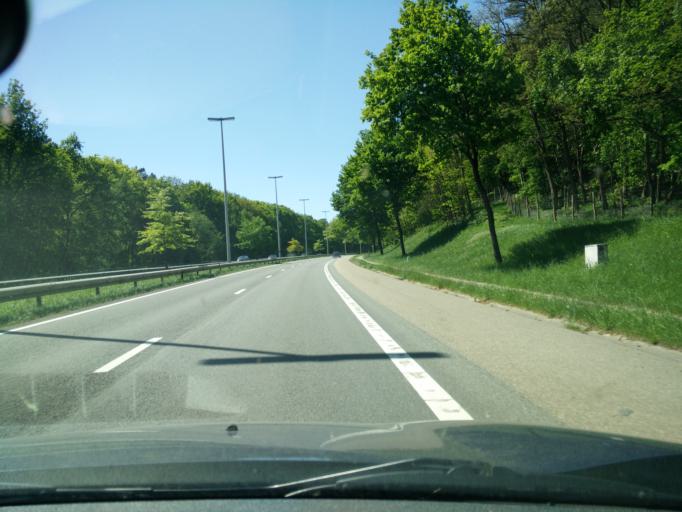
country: BE
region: Flanders
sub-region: Provincie Limburg
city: Maasmechelen
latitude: 51.0125
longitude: 5.6695
